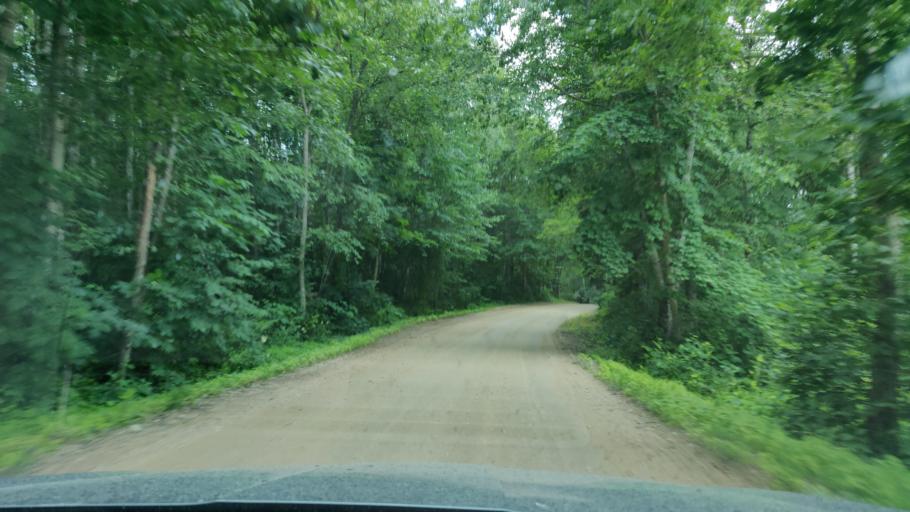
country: EE
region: Vorumaa
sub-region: Antsla vald
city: Vana-Antsla
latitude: 58.0346
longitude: 26.5534
